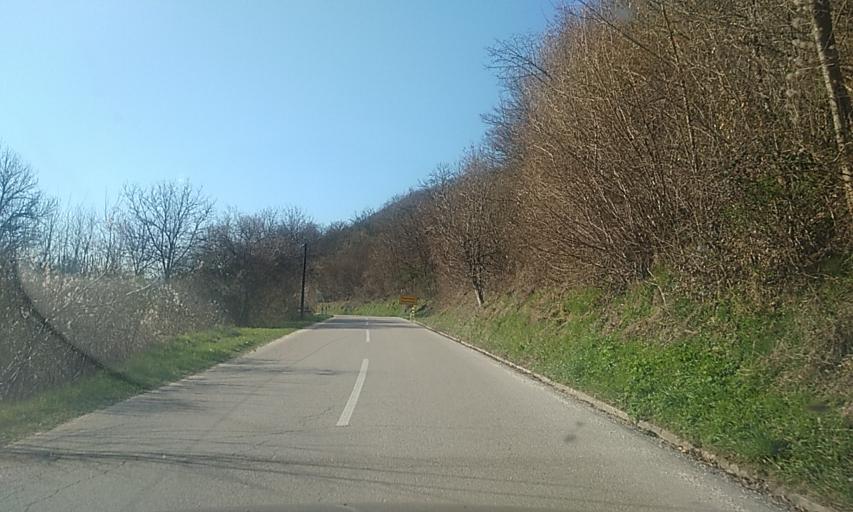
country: RS
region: Central Serbia
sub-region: Pcinjski Okrug
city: Bosilegrad
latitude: 42.4703
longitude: 22.4819
